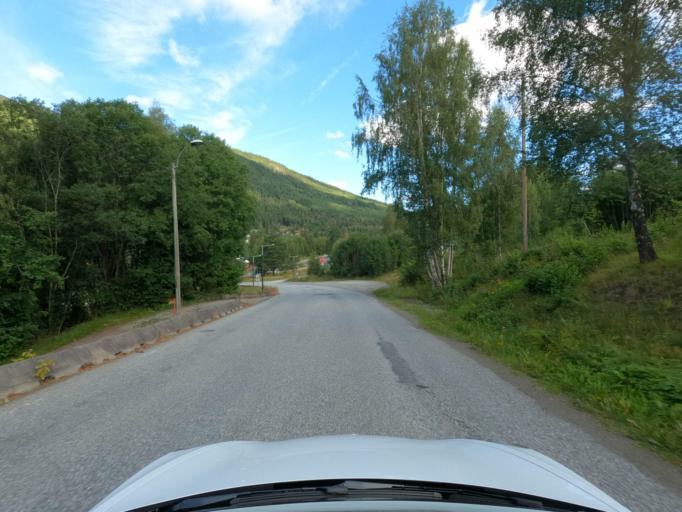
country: NO
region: Telemark
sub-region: Tinn
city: Rjukan
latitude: 59.9947
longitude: 8.8295
